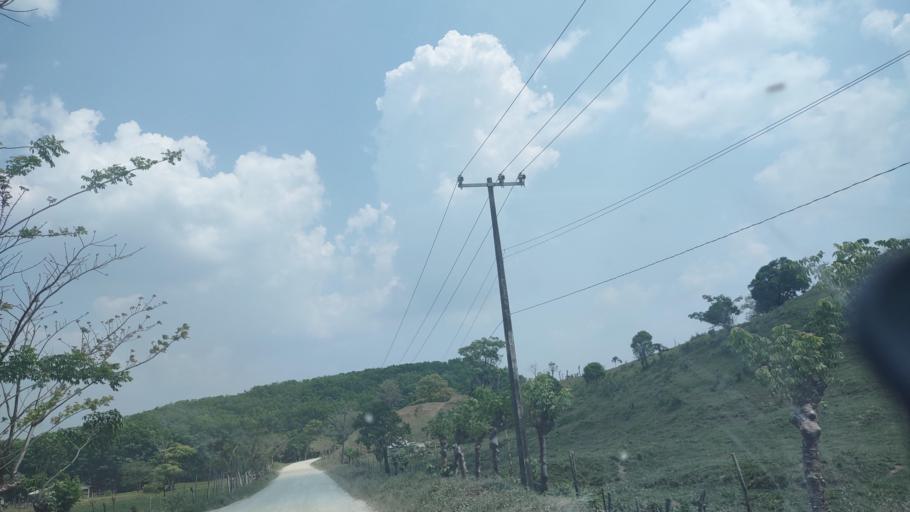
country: MX
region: Tabasco
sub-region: Huimanguillo
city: Francisco Rueda
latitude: 17.6066
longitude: -93.9070
